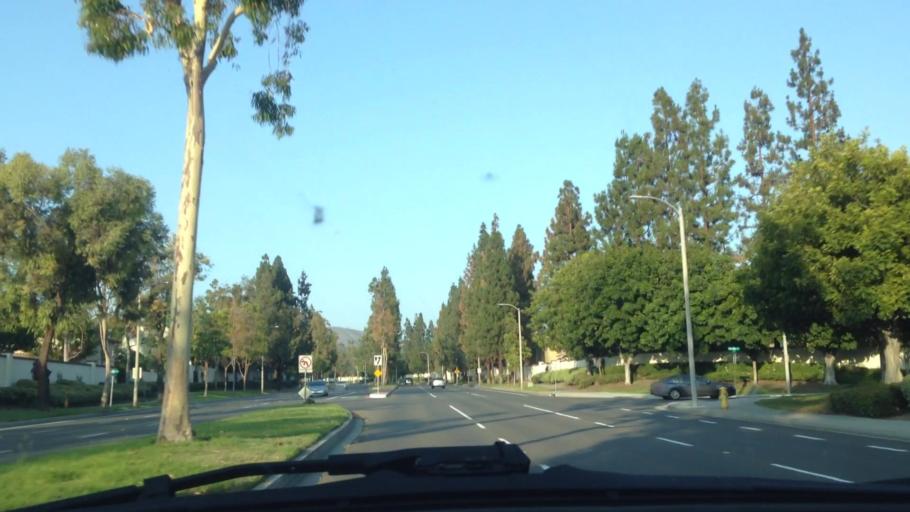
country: US
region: California
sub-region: Orange County
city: North Tustin
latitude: 33.7448
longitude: -117.7834
